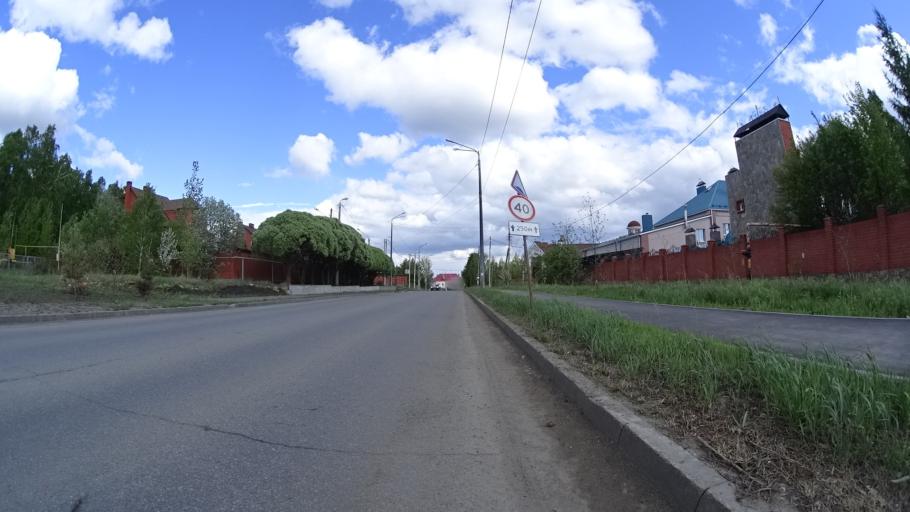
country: RU
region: Chelyabinsk
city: Sargazy
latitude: 55.1529
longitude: 61.2678
